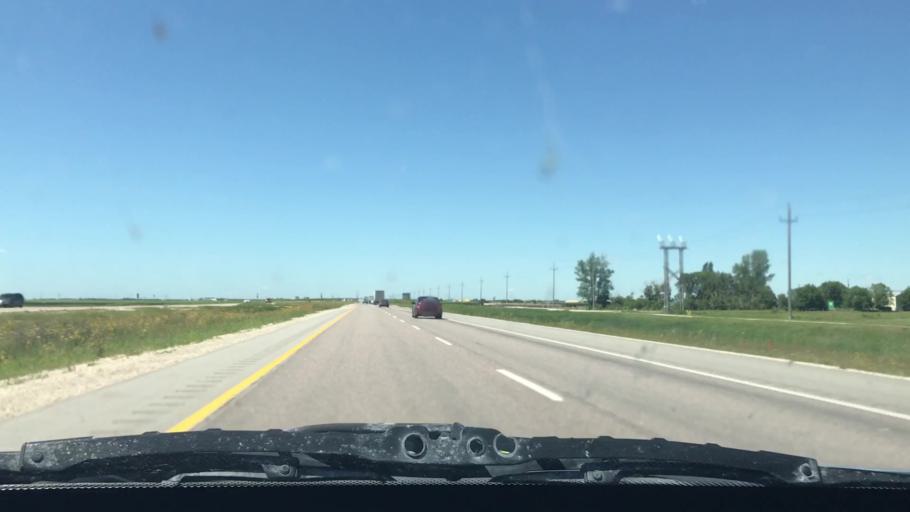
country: CA
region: Manitoba
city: Steinbach
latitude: 49.6890
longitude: -96.6155
